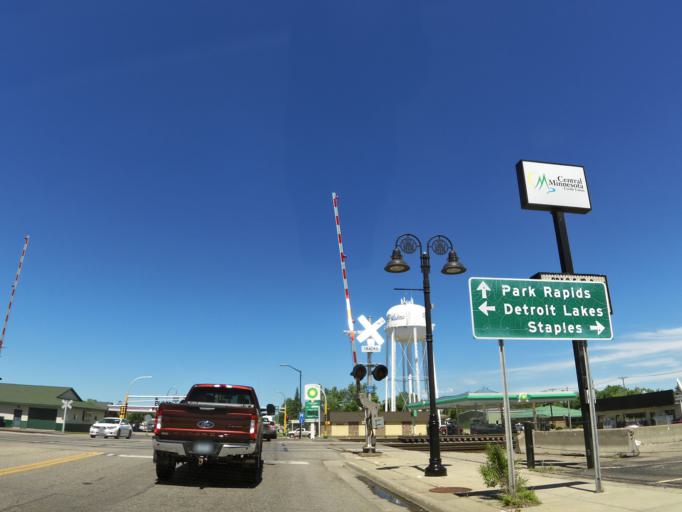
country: US
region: Minnesota
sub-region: Wadena County
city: Wadena
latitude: 46.4414
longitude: -95.1366
